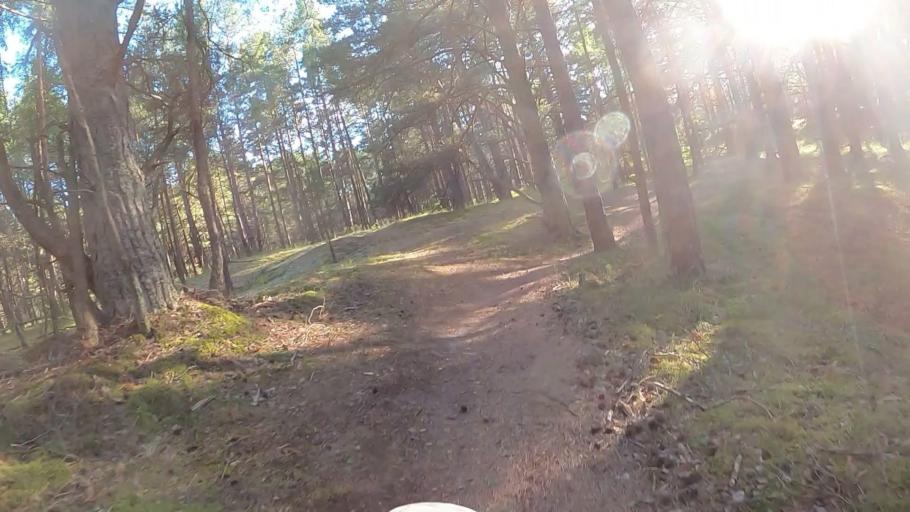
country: LV
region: Carnikava
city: Carnikava
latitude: 57.1338
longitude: 24.2318
